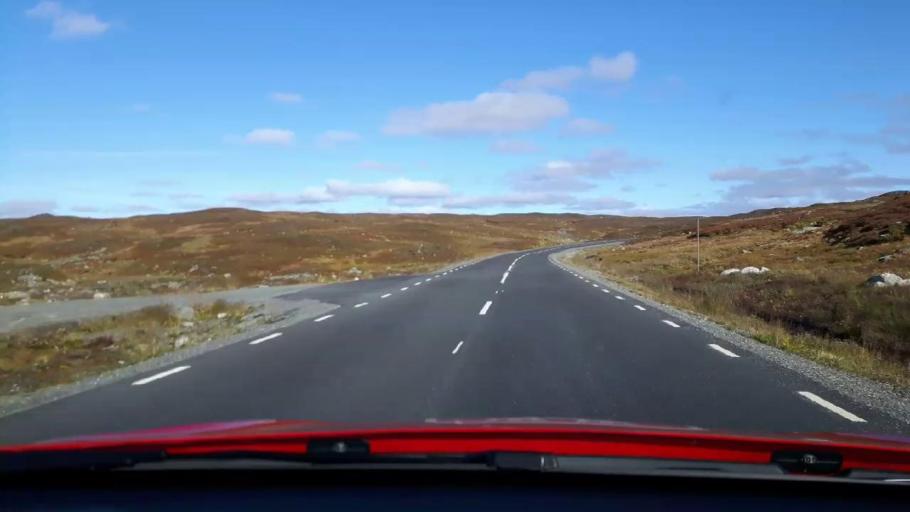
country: NO
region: Nordland
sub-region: Hattfjelldal
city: Hattfjelldal
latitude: 65.0463
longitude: 14.3336
